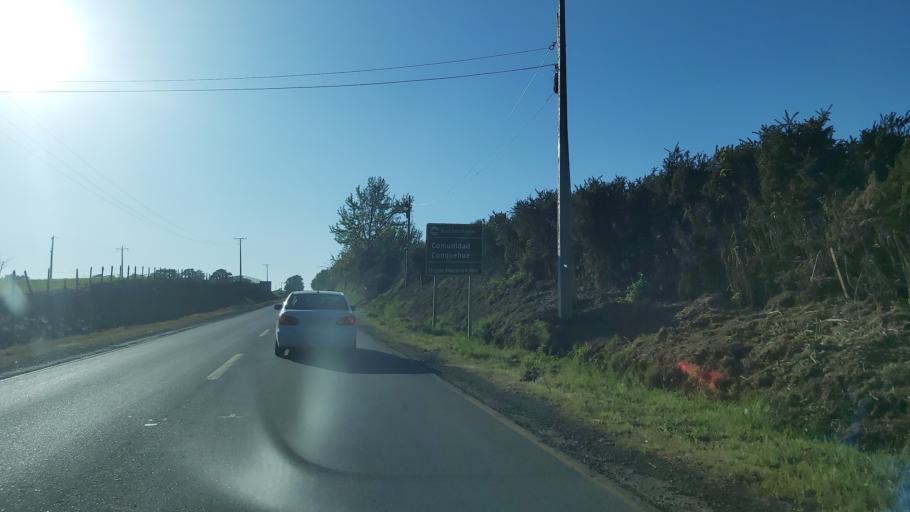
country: CL
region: Araucania
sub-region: Provincia de Malleco
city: Victoria
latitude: -38.2580
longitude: -72.2619
